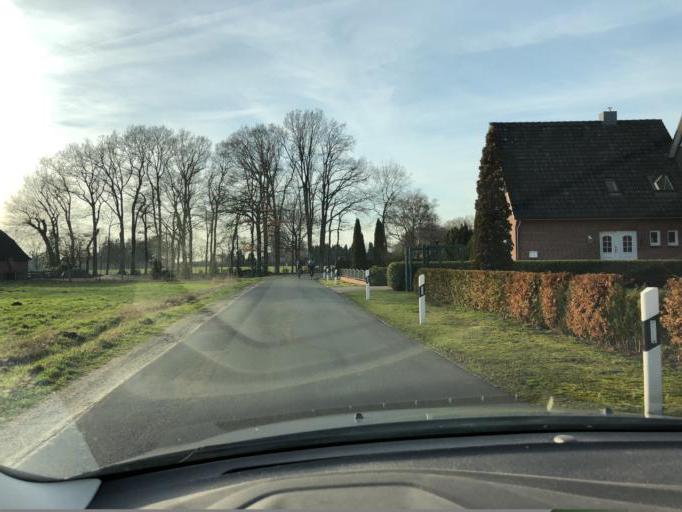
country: DE
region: Lower Saxony
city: Bad Zwischenahn
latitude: 53.1724
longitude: 8.0580
